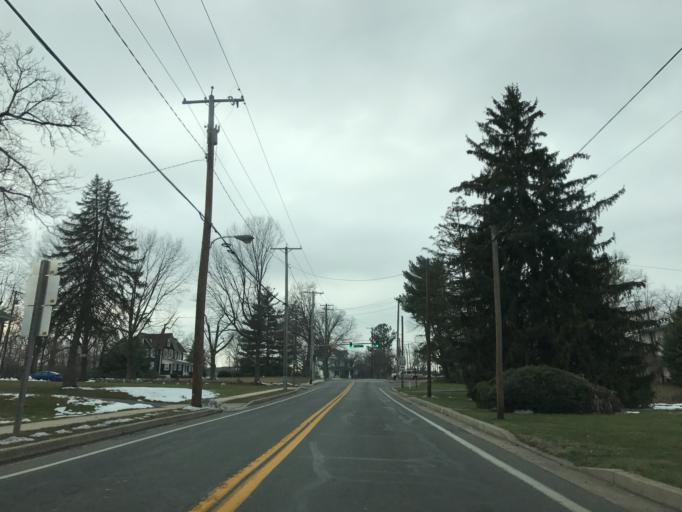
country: US
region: Maryland
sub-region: Harford County
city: Aberdeen
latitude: 39.5131
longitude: -76.1737
